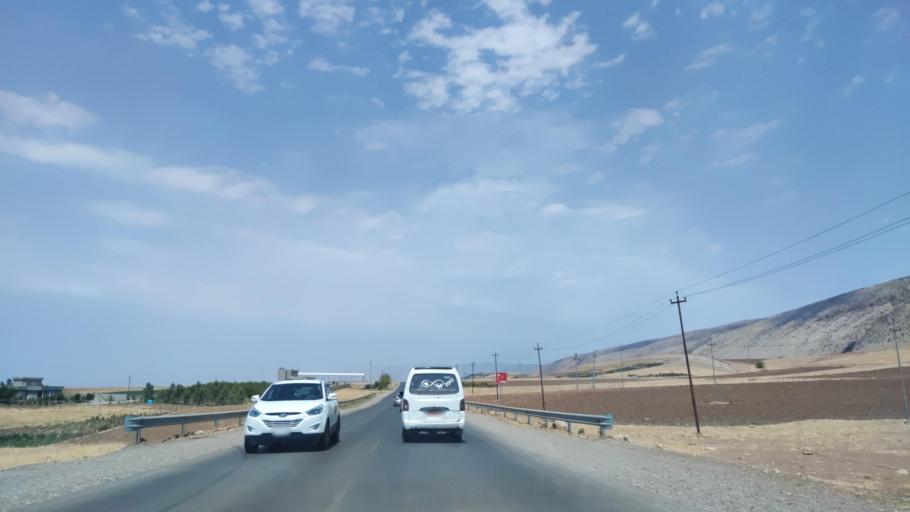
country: IQ
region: Arbil
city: Shaqlawah
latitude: 36.5122
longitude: 44.3758
